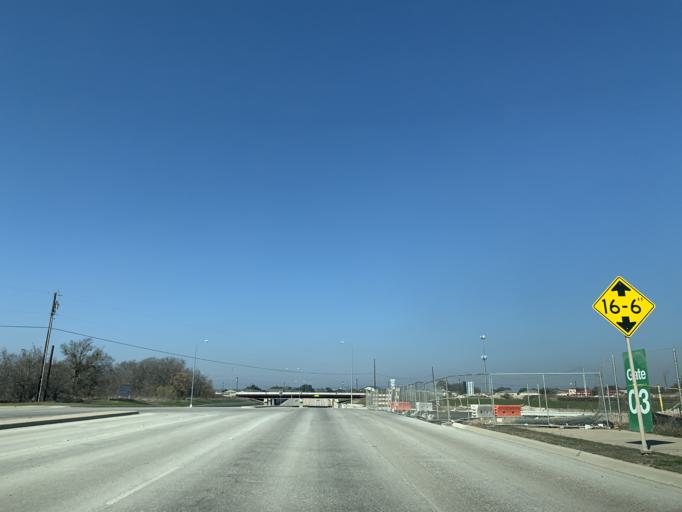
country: US
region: Texas
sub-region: Williamson County
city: Round Rock
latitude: 30.5193
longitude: -97.6384
